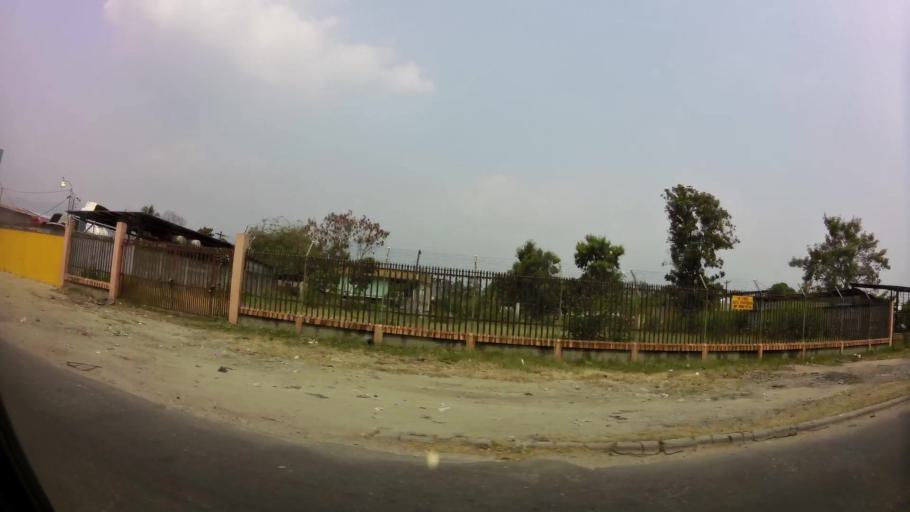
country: HN
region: Cortes
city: San Pedro Sula
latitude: 15.4764
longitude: -88.0081
